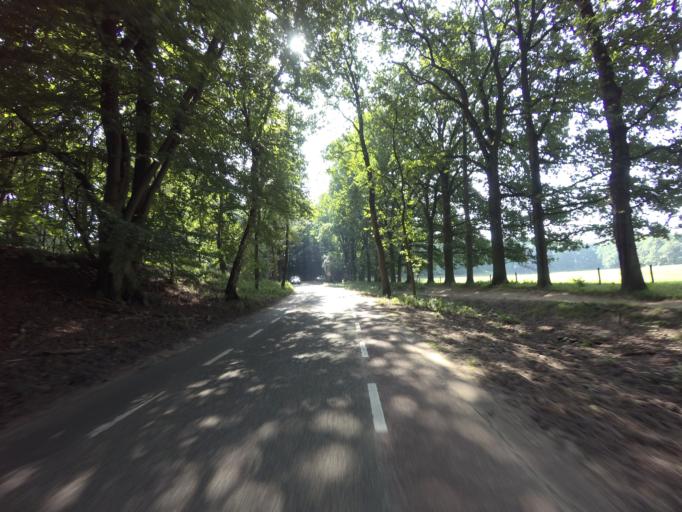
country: NL
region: Gelderland
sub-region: Gemeente Rheden
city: Rheden
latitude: 52.0203
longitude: 6.0269
